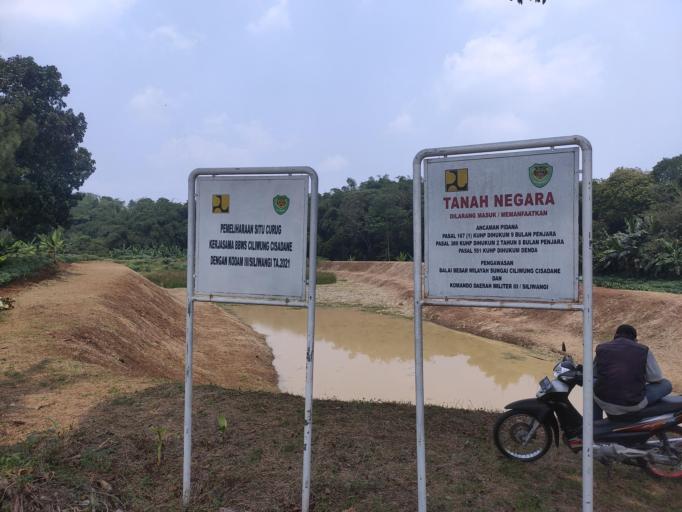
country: ID
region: West Java
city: Parung
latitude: -6.3875
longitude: 106.7270
